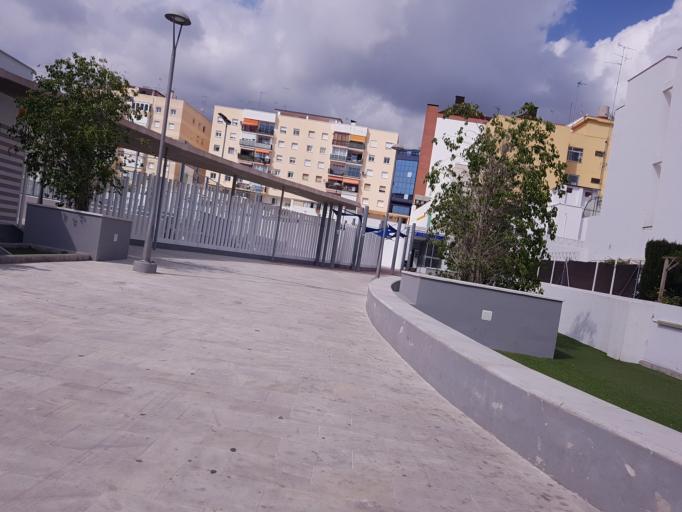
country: ES
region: Andalusia
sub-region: Provincia de Malaga
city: Marbella
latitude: 36.5085
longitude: -4.8891
